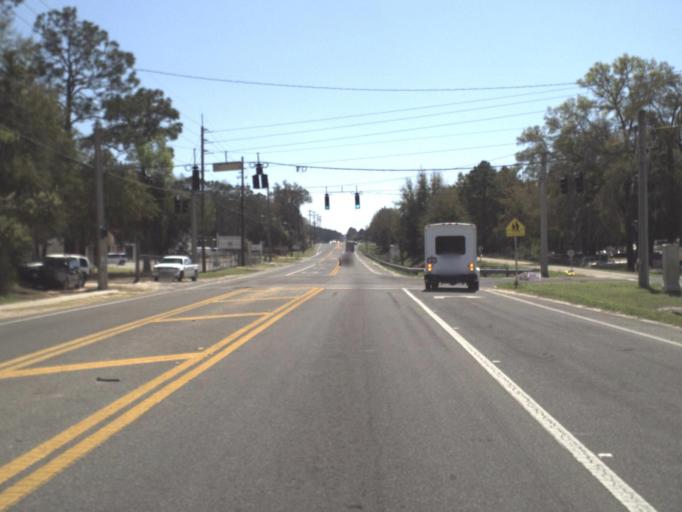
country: US
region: Florida
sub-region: Leon County
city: Tallahassee
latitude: 30.3820
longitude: -84.2730
